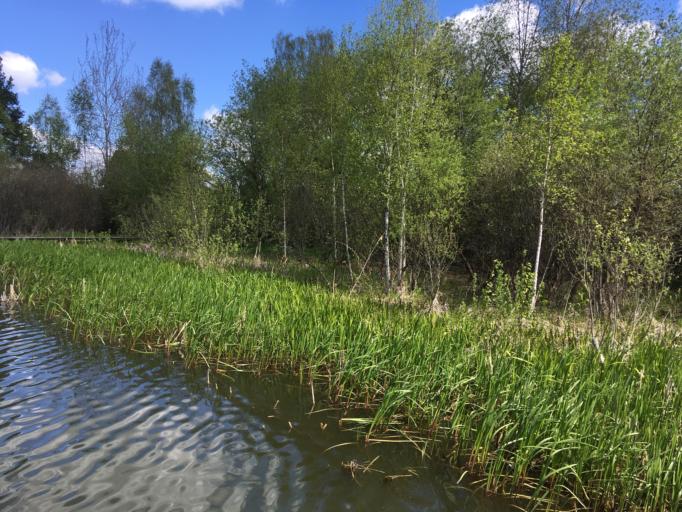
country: BY
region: Minsk
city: Horad Barysaw
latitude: 54.3290
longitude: 28.4368
